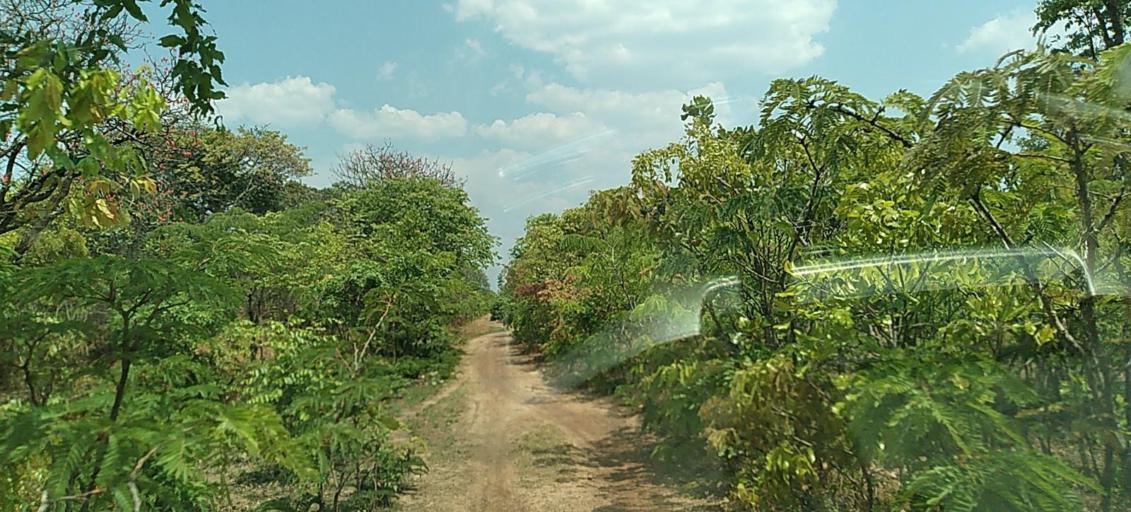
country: CD
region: Katanga
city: Kipushi
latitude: -12.0110
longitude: 27.4316
